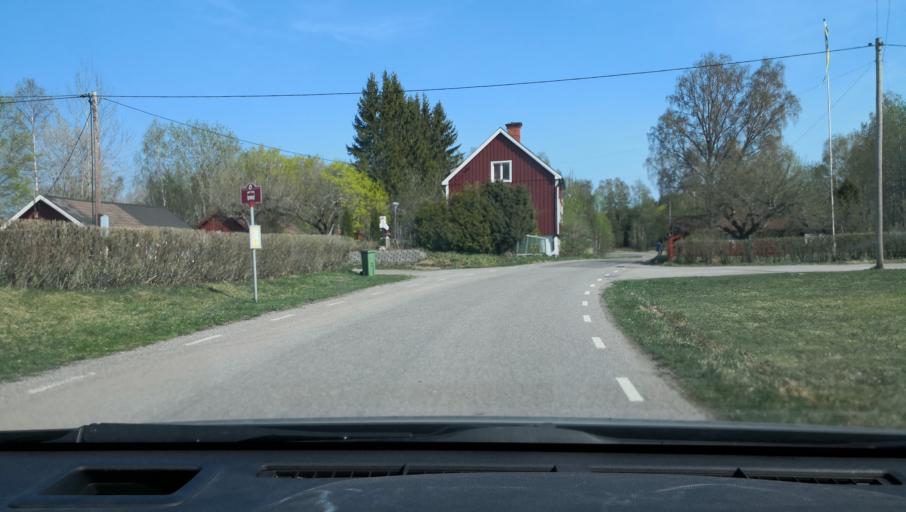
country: SE
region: Uppsala
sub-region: Heby Kommun
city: Heby
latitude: 60.0352
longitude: 16.8078
